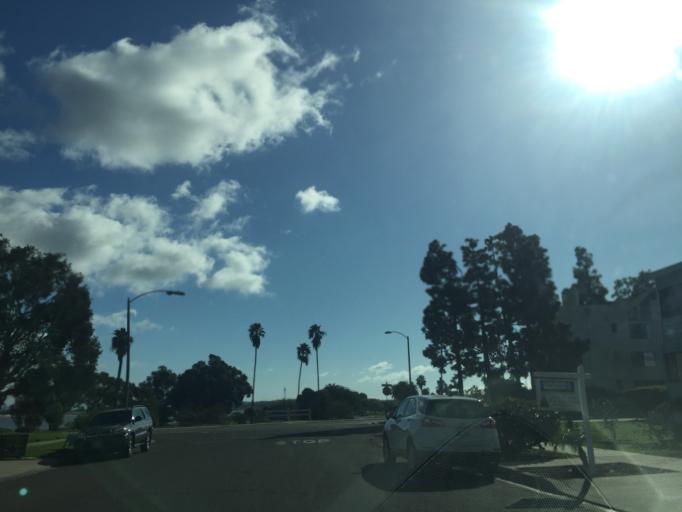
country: US
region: California
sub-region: San Diego County
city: La Jolla
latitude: 32.7899
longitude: -117.2340
